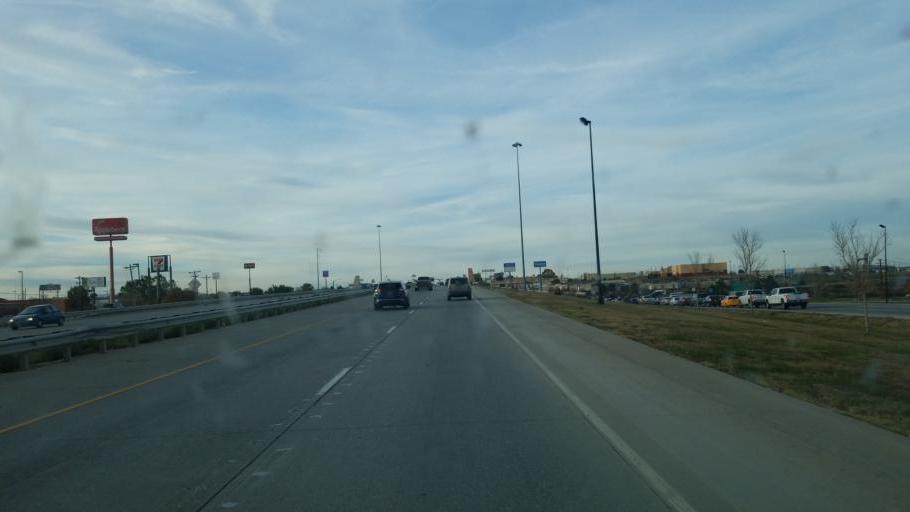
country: US
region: Colorado
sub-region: Pueblo County
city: Pueblo
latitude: 38.3049
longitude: -104.6130
